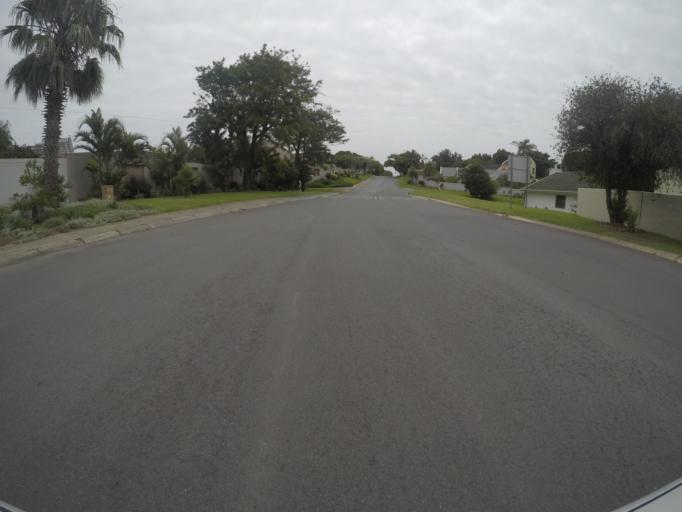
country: ZA
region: Eastern Cape
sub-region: Buffalo City Metropolitan Municipality
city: East London
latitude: -32.9790
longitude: 27.9480
